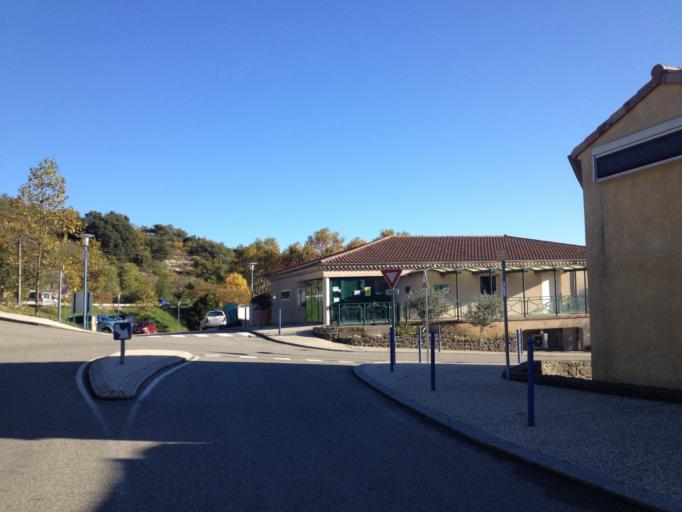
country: FR
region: Rhone-Alpes
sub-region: Departement de l'Ardeche
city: Alissas
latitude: 44.7145
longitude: 4.6325
